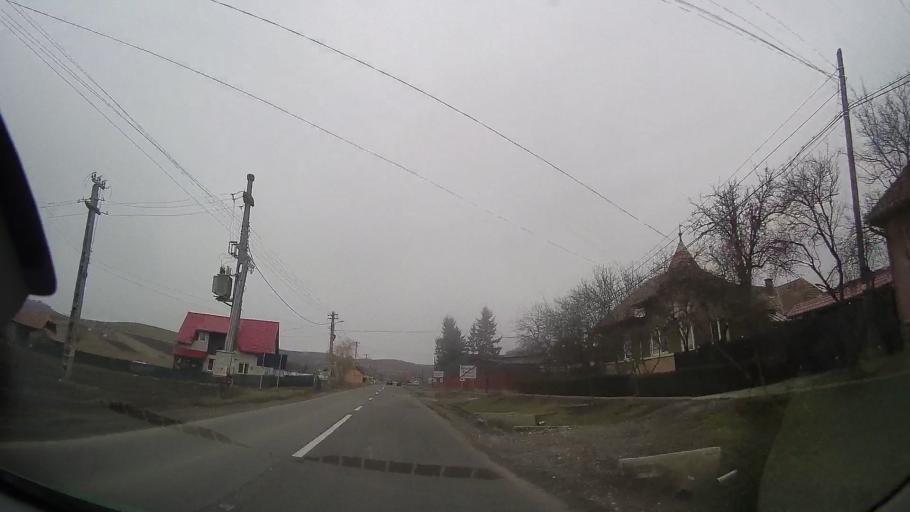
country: RO
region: Mures
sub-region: Comuna Ceausu de Campie
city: Ceausu de Campie
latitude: 46.6457
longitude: 24.4974
